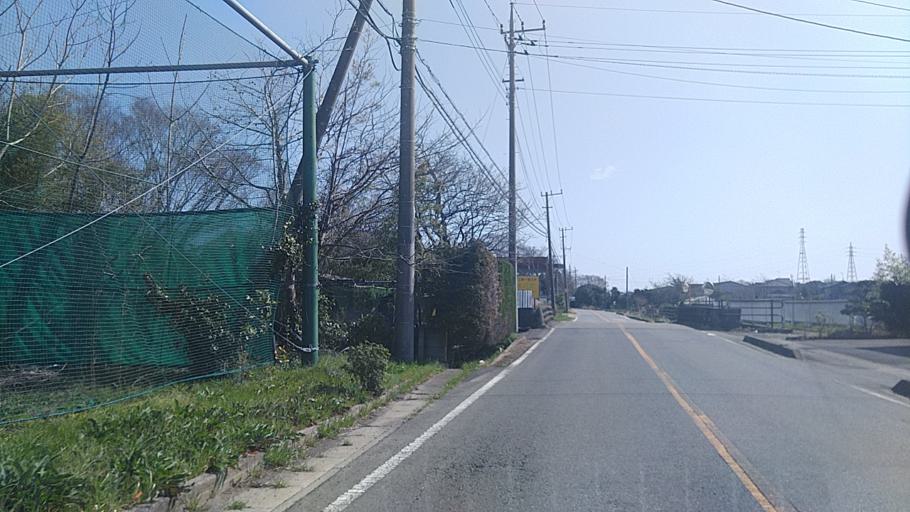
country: JP
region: Ibaraki
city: Ryugasaki
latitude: 35.8625
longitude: 140.1853
